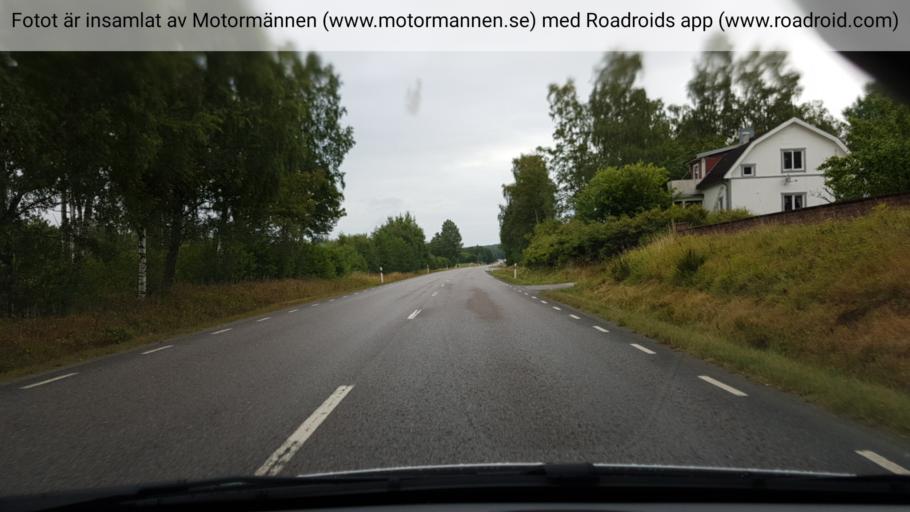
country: SE
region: Vaestra Goetaland
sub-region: Karlsborgs Kommun
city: Molltorp
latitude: 58.4717
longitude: 14.3189
